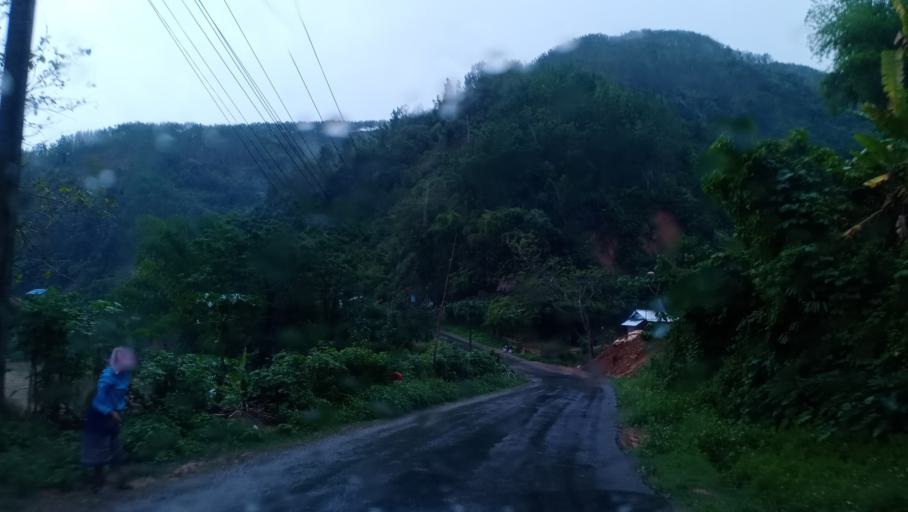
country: LA
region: Phongsali
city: Khoa
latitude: 21.0663
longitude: 102.4888
